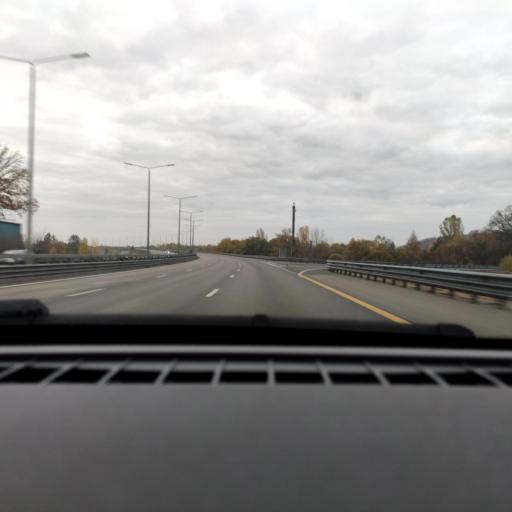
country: RU
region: Voronezj
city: Somovo
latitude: 51.7984
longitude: 39.2572
